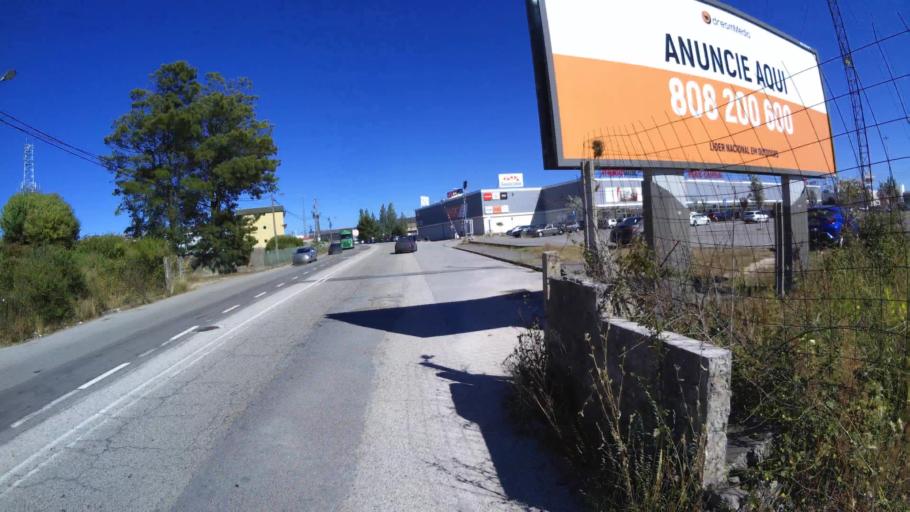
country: PT
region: Aveiro
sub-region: Aveiro
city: Aveiro
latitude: 40.6525
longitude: -8.6145
